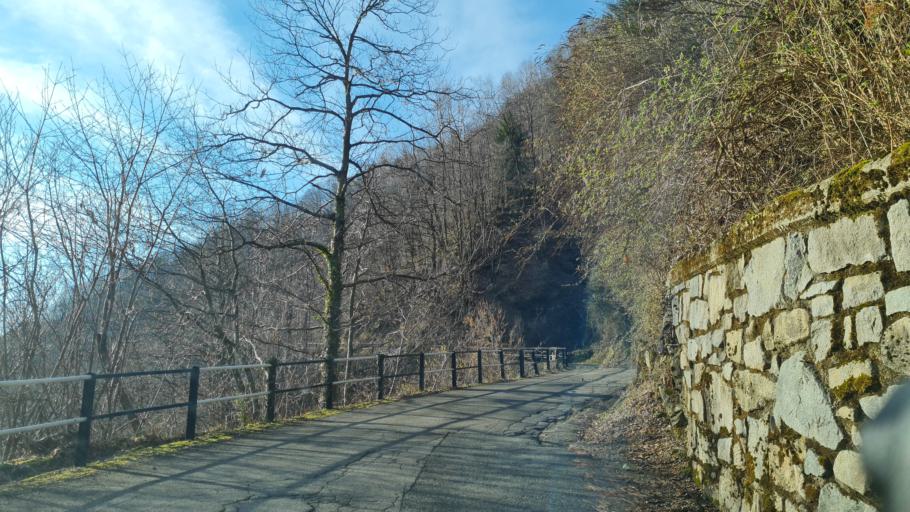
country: IT
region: Piedmont
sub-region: Provincia di Biella
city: San Paolo Cervo
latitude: 45.6467
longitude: 8.0164
